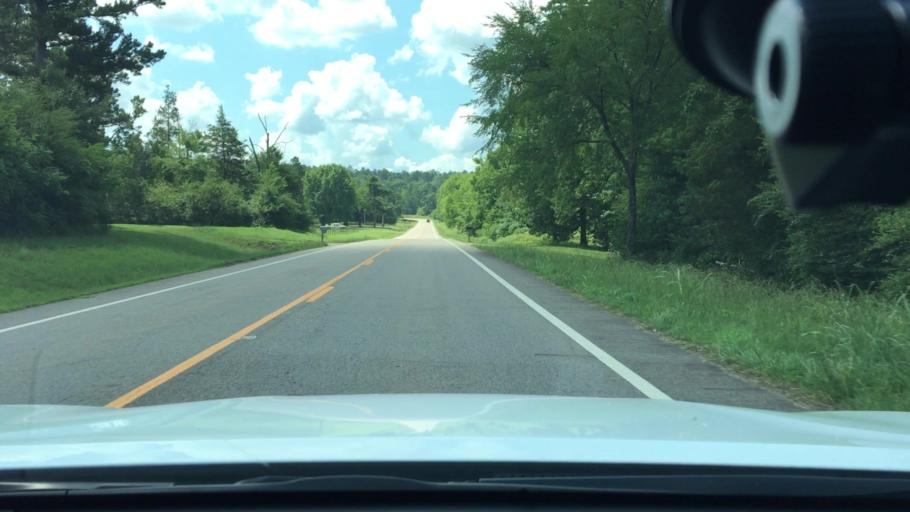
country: US
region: Arkansas
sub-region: Logan County
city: Paris
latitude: 35.2632
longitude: -93.6832
